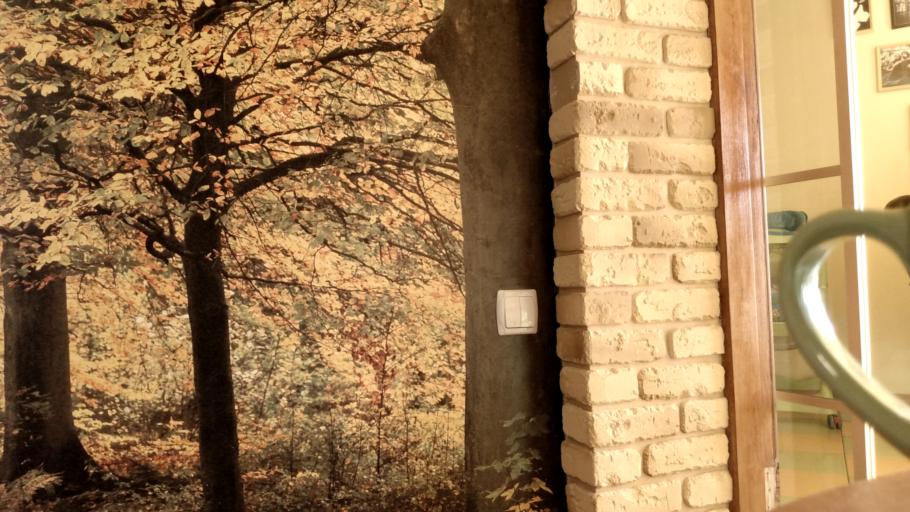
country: RU
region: Vologda
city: Imeni Zhelyabova
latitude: 58.8216
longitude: 36.8756
